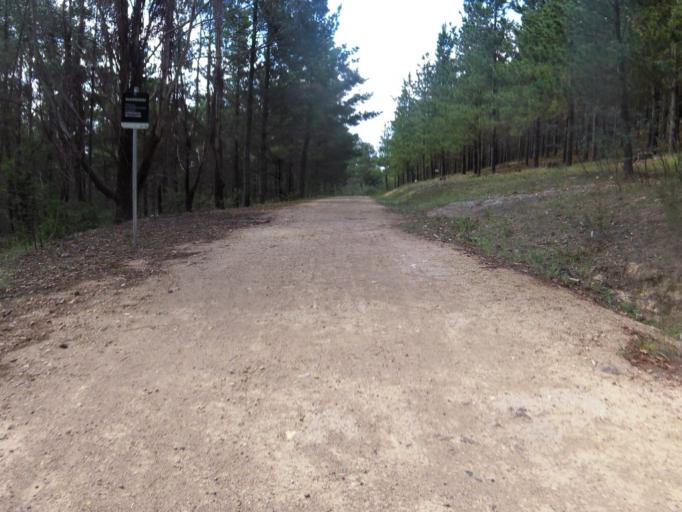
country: AU
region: Australian Capital Territory
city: Macarthur
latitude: -35.3841
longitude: 149.1211
